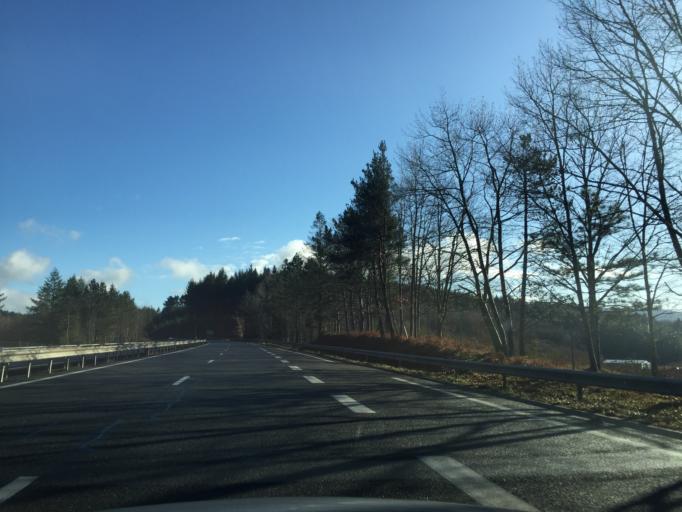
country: FR
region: Auvergne
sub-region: Departement du Puy-de-Dome
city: Celles-sur-Durolle
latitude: 45.8799
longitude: 3.6295
